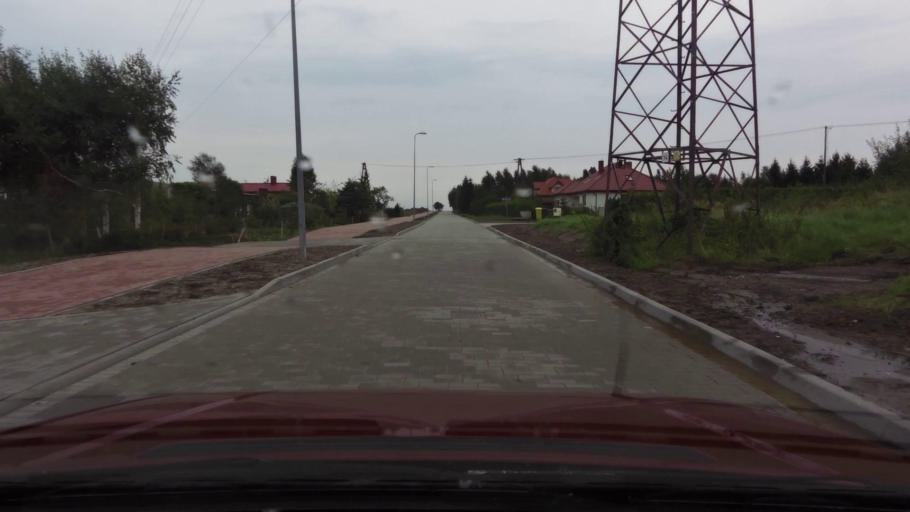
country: PL
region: West Pomeranian Voivodeship
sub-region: Powiat kolobrzeski
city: Grzybowo
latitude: 54.1423
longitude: 15.5305
